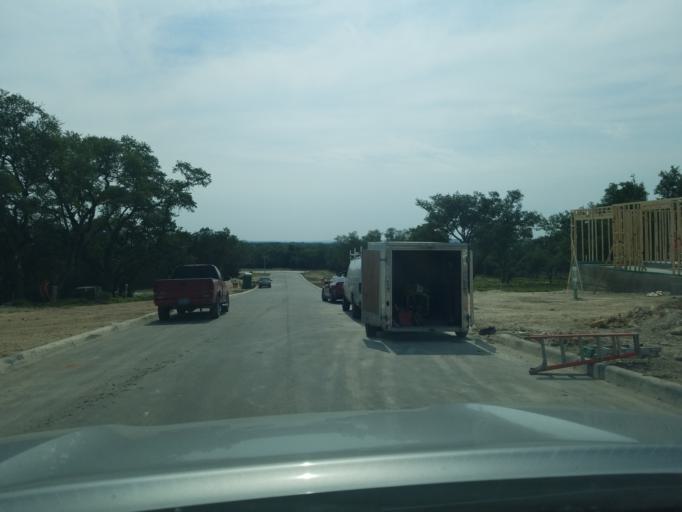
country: US
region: Texas
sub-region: Kendall County
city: Boerne
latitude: 29.7506
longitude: -98.7164
